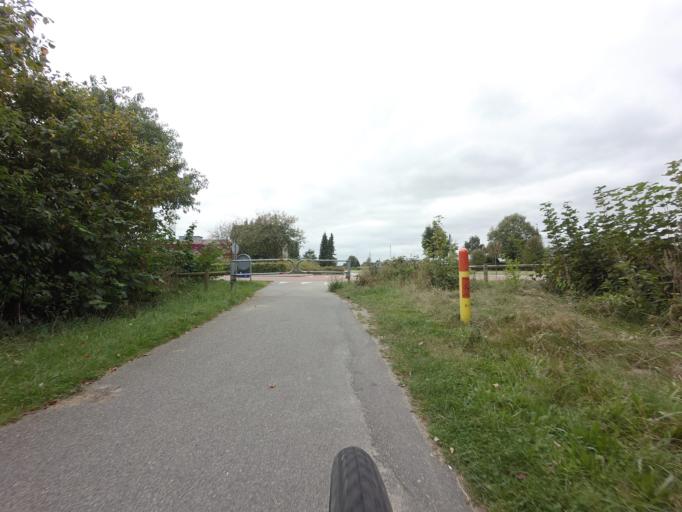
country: DK
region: South Denmark
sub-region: Billund Kommune
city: Grindsted
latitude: 55.7653
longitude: 8.9170
